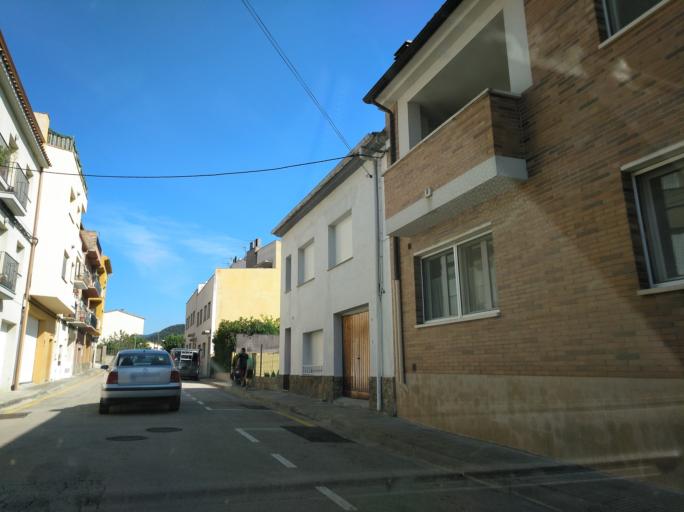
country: ES
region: Catalonia
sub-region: Provincia de Girona
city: la Cellera de Ter
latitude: 42.0109
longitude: 2.5998
